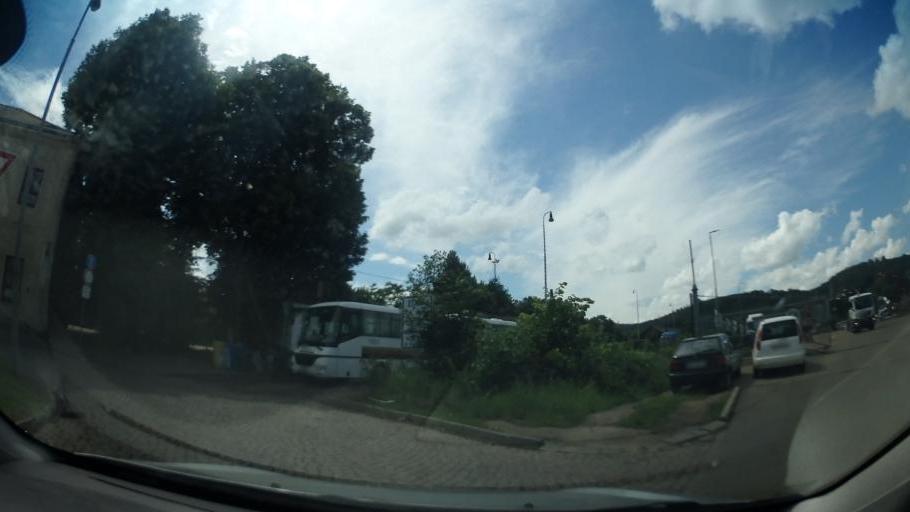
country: CZ
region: South Moravian
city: Zastavka
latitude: 49.1879
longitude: 16.3590
